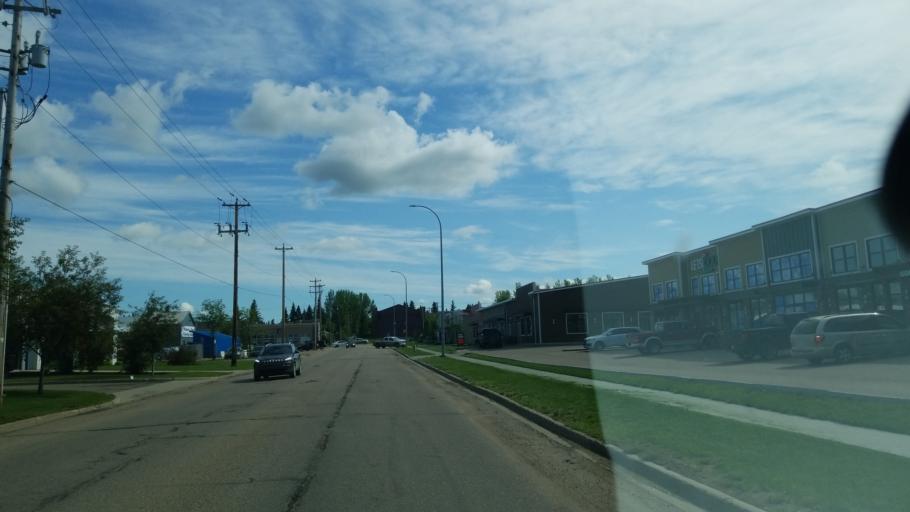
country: CA
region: Saskatchewan
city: Lloydminster
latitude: 53.2726
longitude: -110.0086
